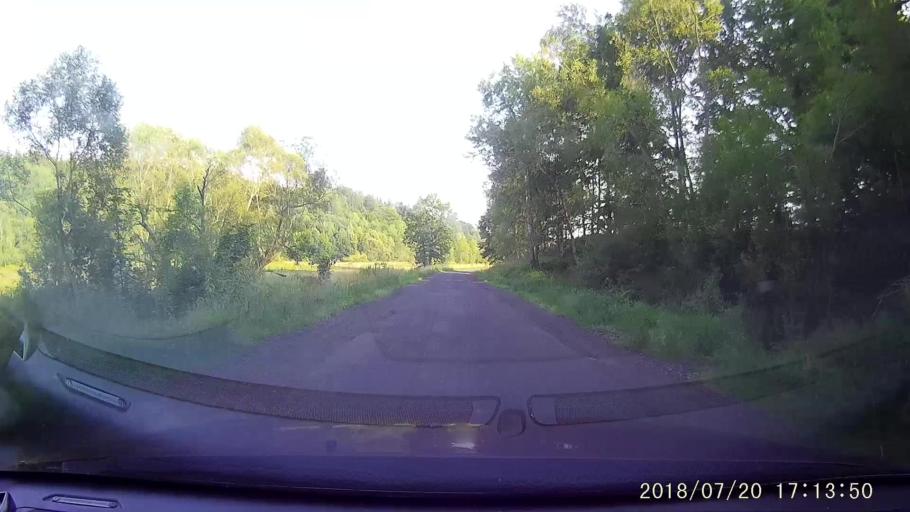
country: PL
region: Lower Silesian Voivodeship
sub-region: Powiat lubanski
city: Lesna
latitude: 51.0129
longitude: 15.2780
